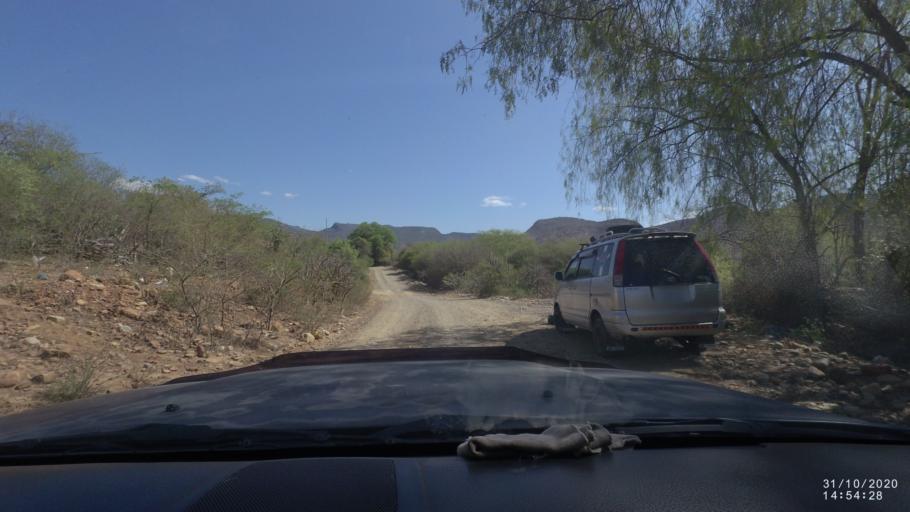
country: BO
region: Cochabamba
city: Aiquile
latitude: -18.2265
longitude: -64.8576
